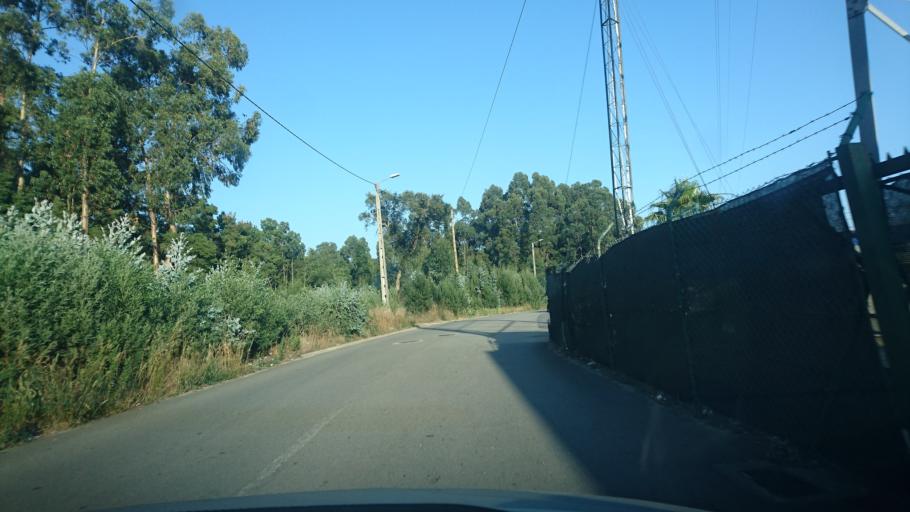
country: PT
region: Aveiro
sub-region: Ovar
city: Esmoriz
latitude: 40.9651
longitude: -8.6118
